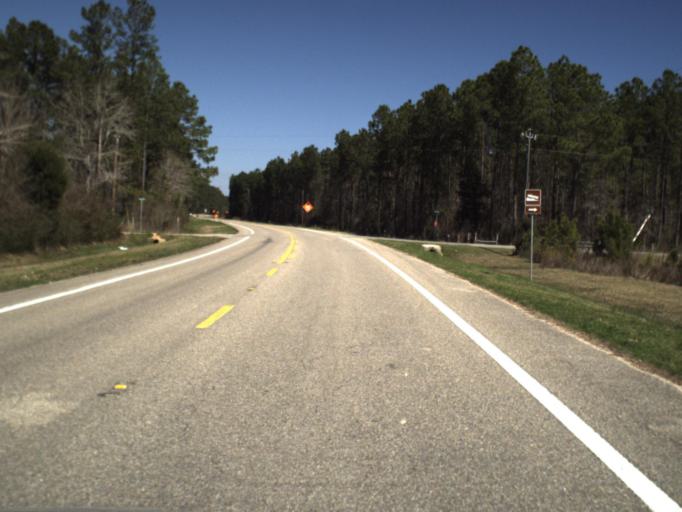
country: US
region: Florida
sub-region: Calhoun County
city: Blountstown
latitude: 30.5181
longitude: -85.0313
